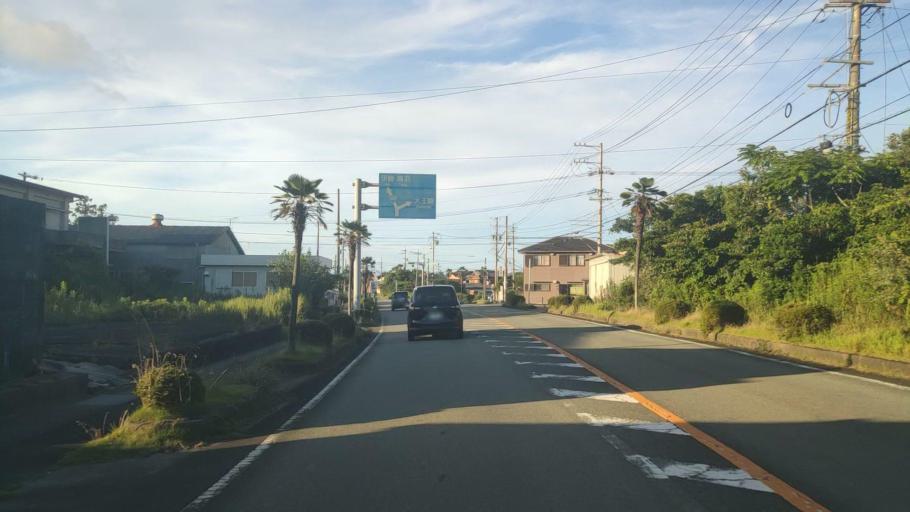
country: JP
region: Mie
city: Toba
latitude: 34.2795
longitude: 136.8800
